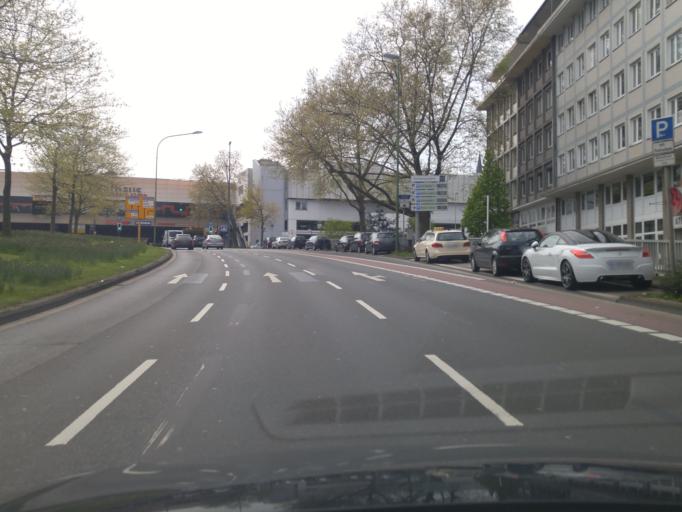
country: DE
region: North Rhine-Westphalia
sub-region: Regierungsbezirk Dusseldorf
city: Essen
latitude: 51.4591
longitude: 7.0145
